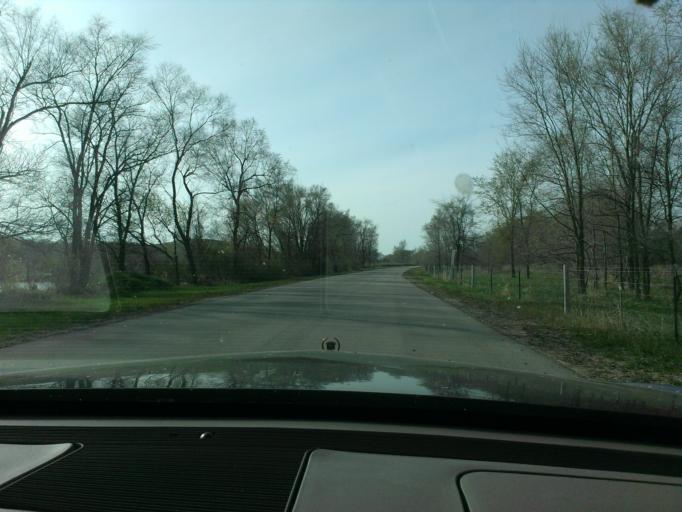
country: US
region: Iowa
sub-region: Linn County
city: Cedar Rapids
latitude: 41.9540
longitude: -91.6355
